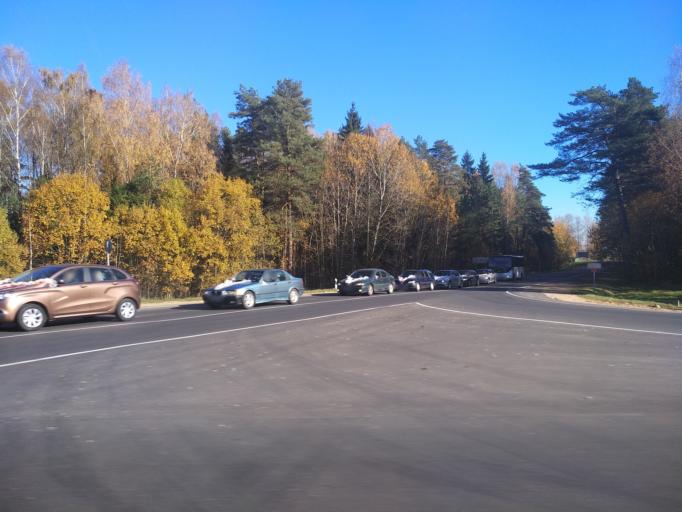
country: BY
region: Minsk
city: Kryvichy
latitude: 54.5887
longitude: 27.1940
